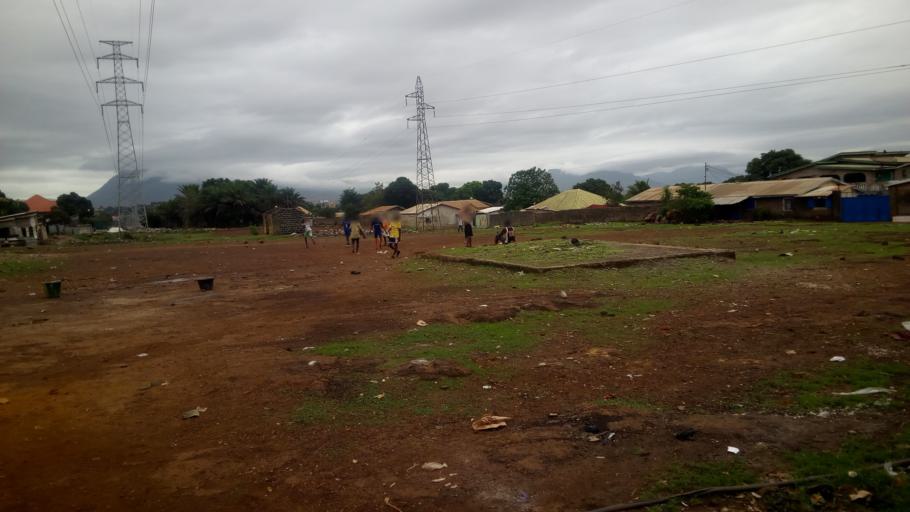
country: GN
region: Kindia
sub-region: Prefecture de Dubreka
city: Dubreka
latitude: 9.6938
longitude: -13.5104
